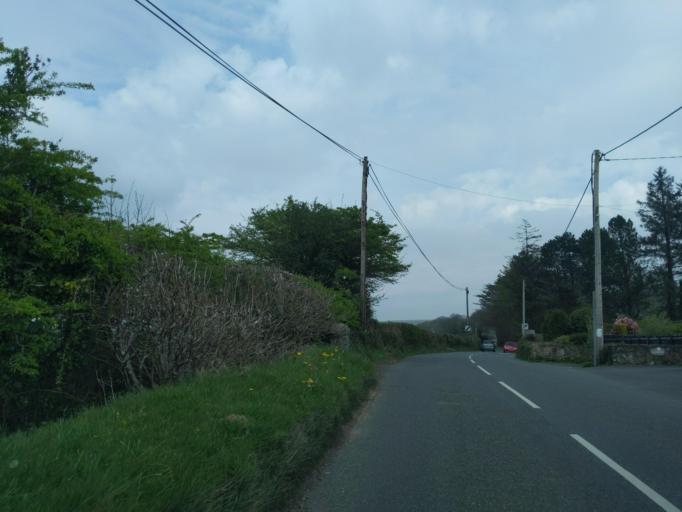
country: GB
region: England
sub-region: Devon
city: Yelverton
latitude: 50.5020
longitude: -4.0634
